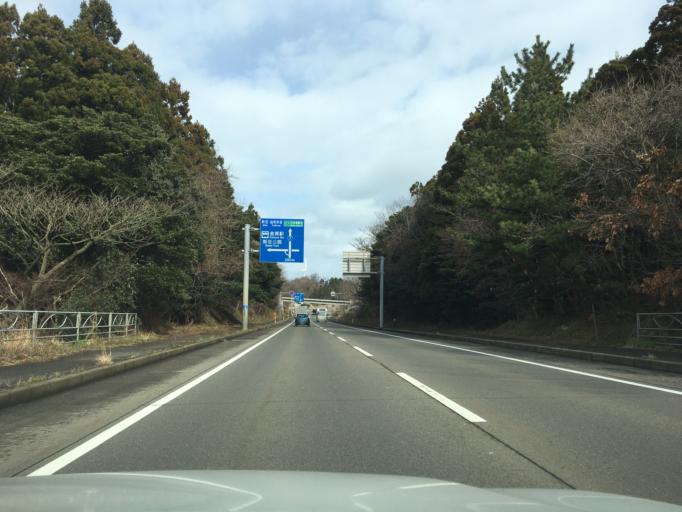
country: JP
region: Yamagata
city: Yuza
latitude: 39.2620
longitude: 139.9250
